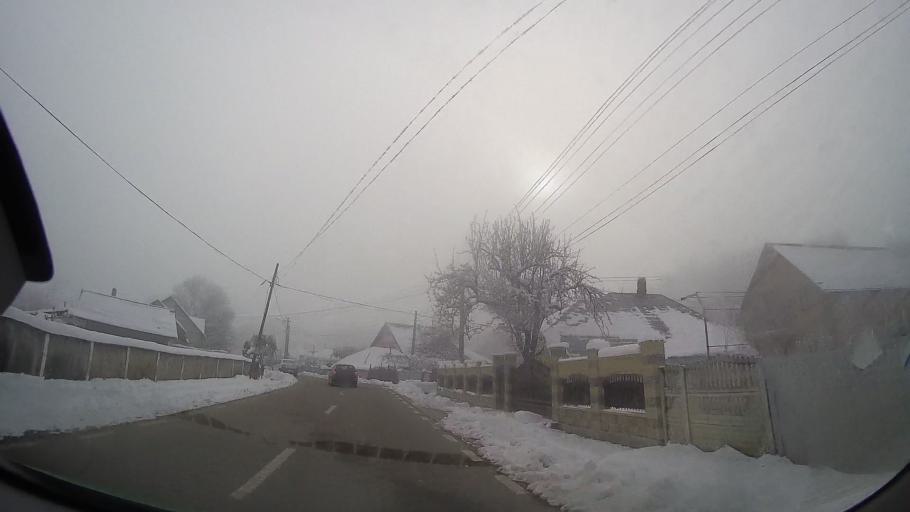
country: RO
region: Iasi
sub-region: Comuna Valea Seaca
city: Valea Seaca
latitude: 47.2883
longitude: 26.6672
